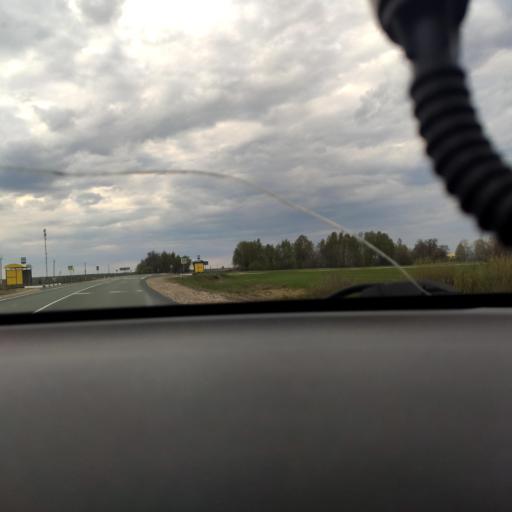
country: RU
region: Mariy-El
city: Krasnogorskiy
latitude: 56.1914
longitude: 48.2397
